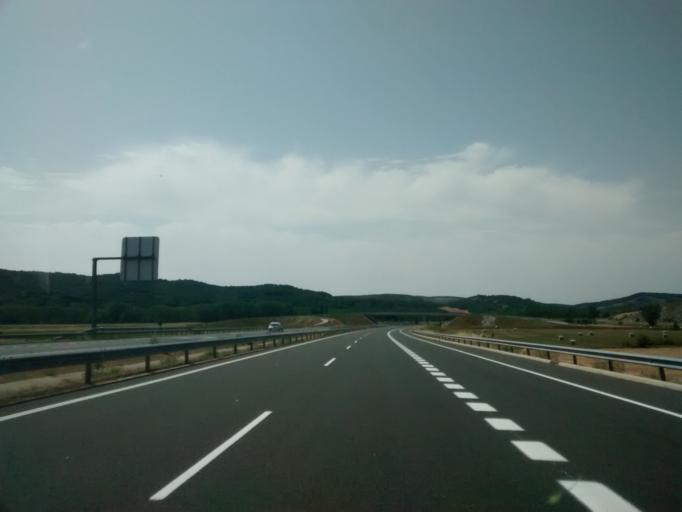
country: ES
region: Castille and Leon
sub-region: Provincia de Palencia
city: Alar del Rey
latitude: 42.7145
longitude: -4.2891
